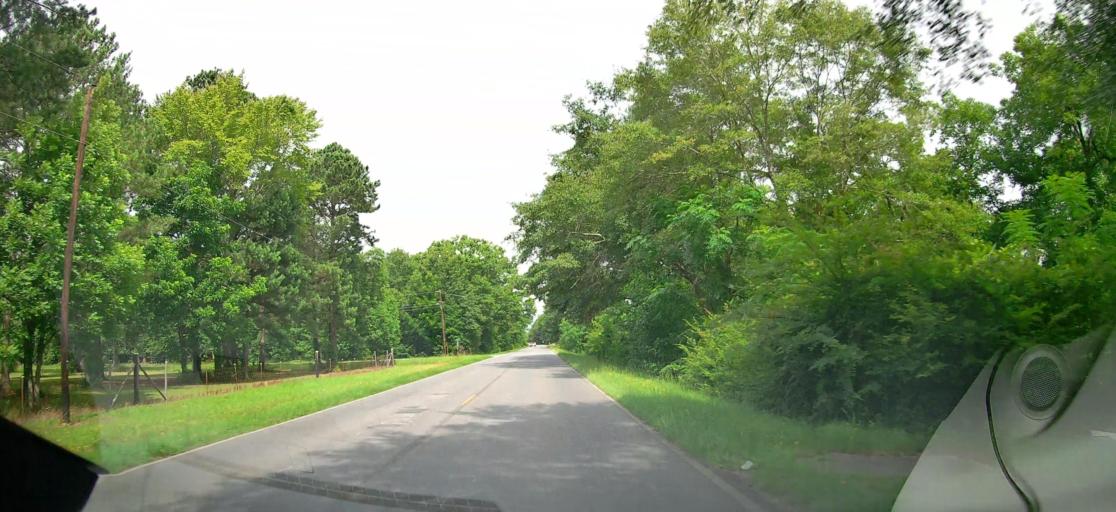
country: US
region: Georgia
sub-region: Peach County
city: Byron
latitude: 32.6444
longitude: -83.7473
